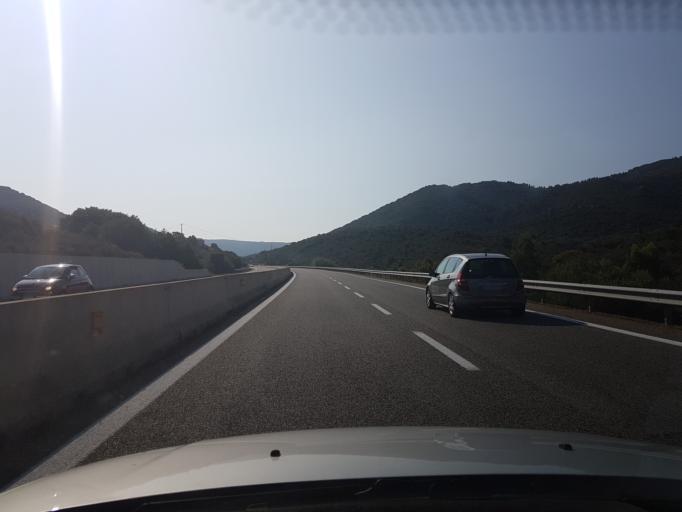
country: IT
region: Sardinia
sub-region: Provincia di Olbia-Tempio
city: Loiri Porto San Paolo
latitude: 40.8340
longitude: 9.5594
